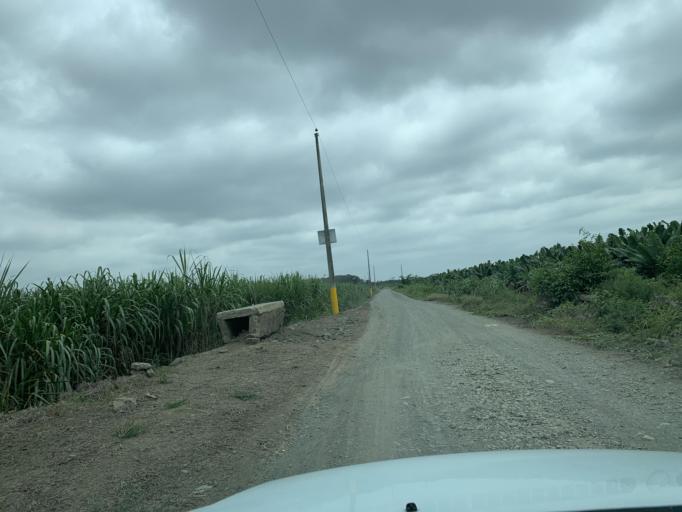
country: EC
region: Guayas
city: Coronel Marcelino Mariduena
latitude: -2.3348
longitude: -79.4555
